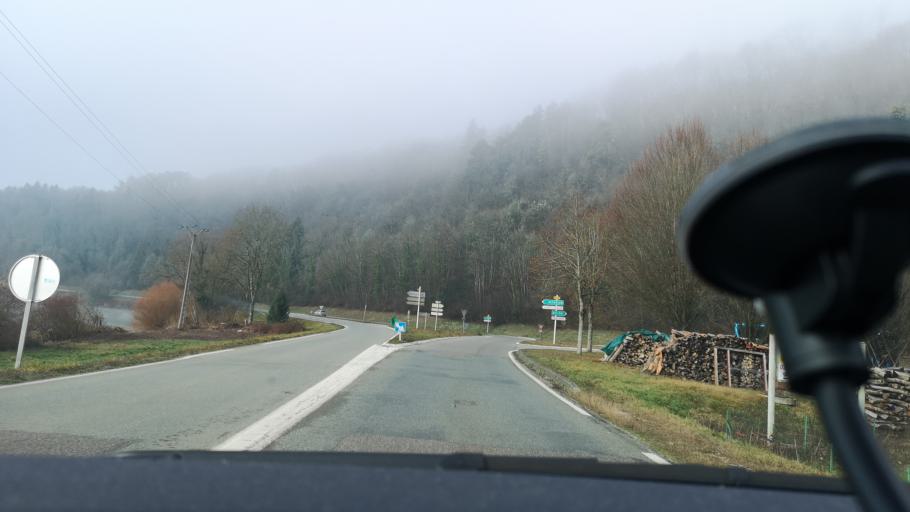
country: FR
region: Franche-Comte
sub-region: Departement du Doubs
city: Montenois
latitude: 47.4575
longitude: 6.5925
